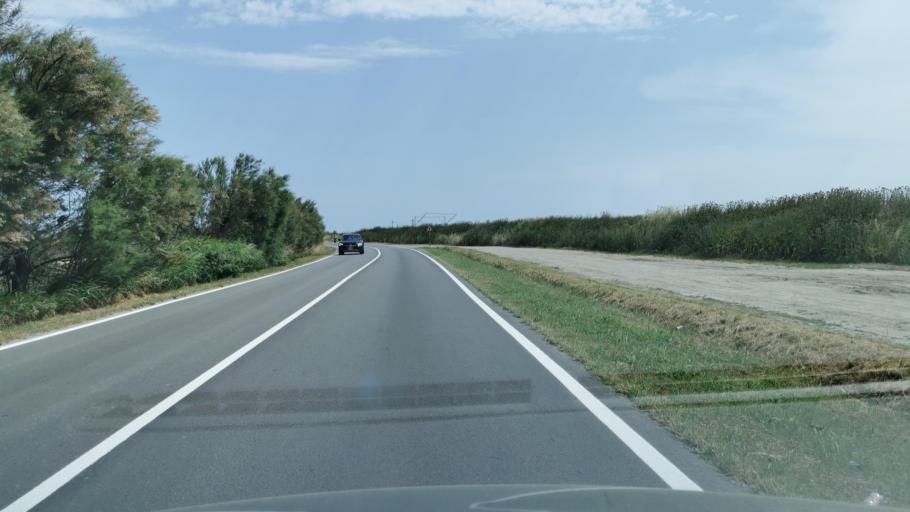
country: IT
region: Emilia-Romagna
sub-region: Provincia di Ferrara
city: Comacchio
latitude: 44.6797
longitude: 12.2018
